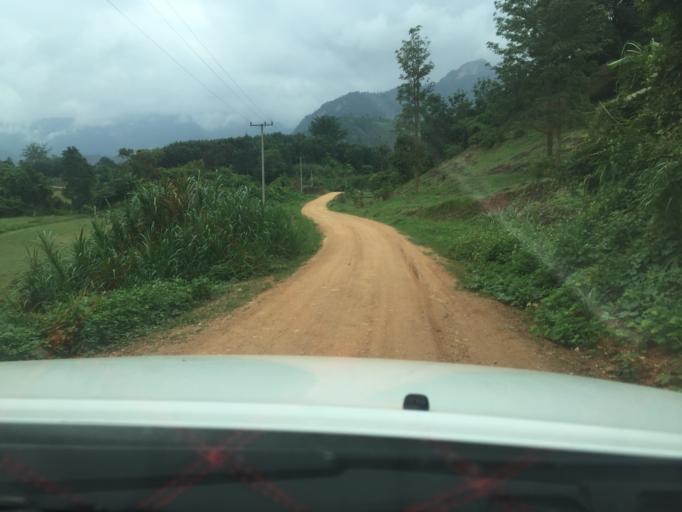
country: TH
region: Phayao
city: Phu Sang
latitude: 19.7350
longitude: 100.4774
